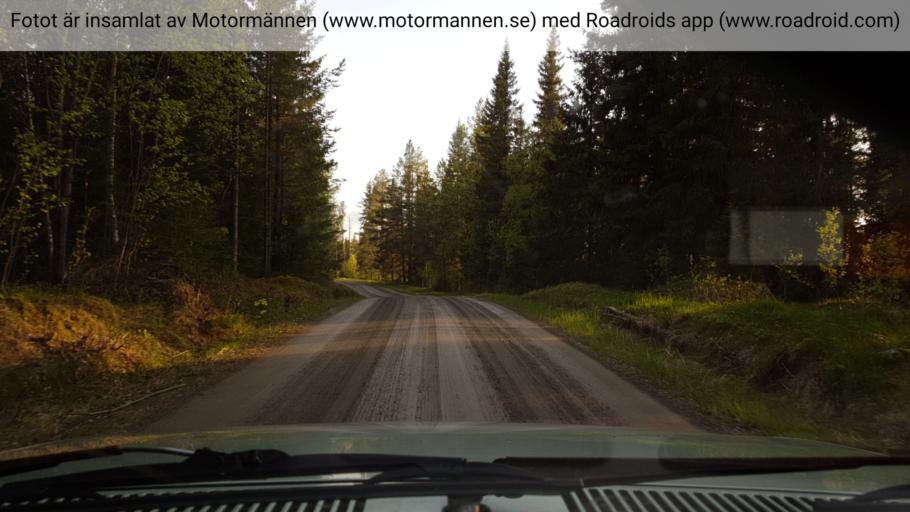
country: SE
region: Jaemtland
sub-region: Bergs Kommun
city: Hoverberg
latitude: 62.9553
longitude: 14.5402
